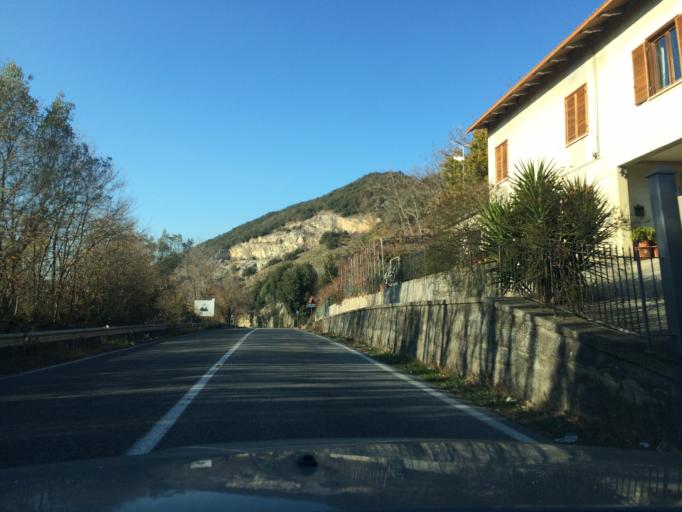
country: IT
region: Umbria
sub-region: Provincia di Terni
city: Fornole
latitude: 42.5397
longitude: 12.4683
